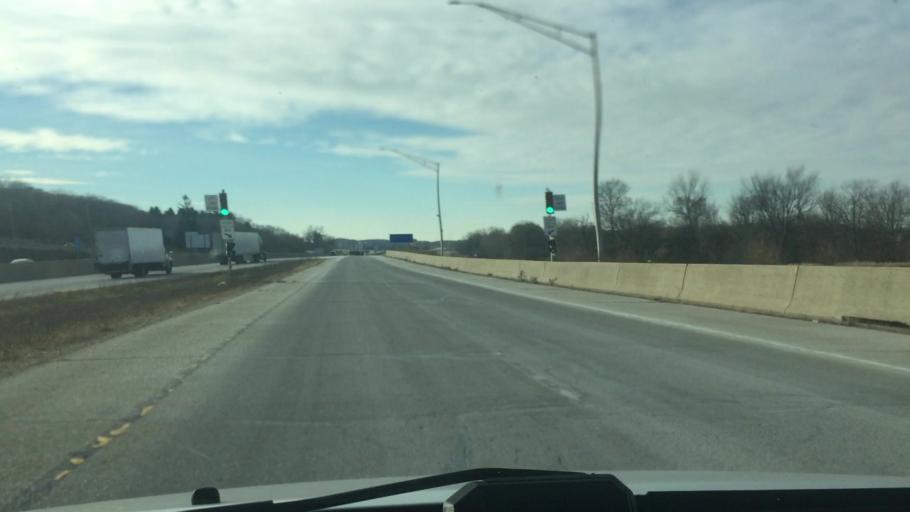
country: US
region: Wisconsin
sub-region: Waukesha County
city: Pewaukee
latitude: 43.0500
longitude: -88.2886
